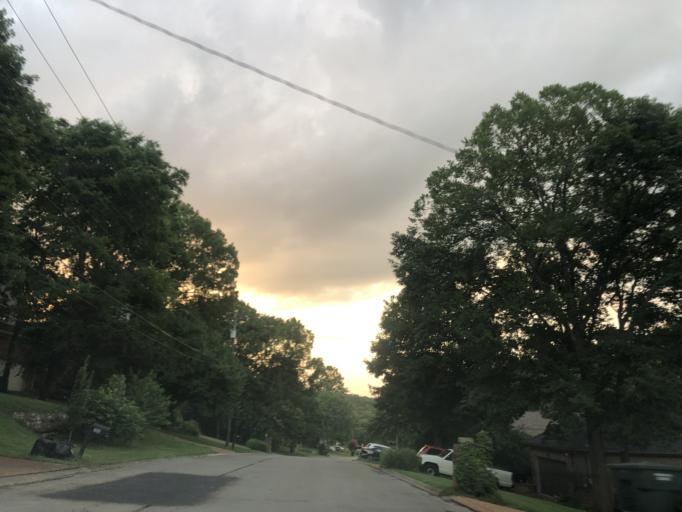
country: US
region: Tennessee
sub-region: Davidson County
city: Lakewood
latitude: 36.1454
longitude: -86.6343
